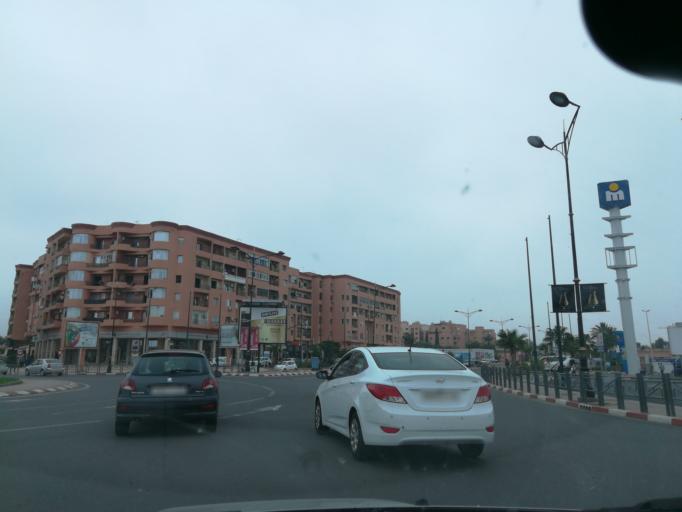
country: MA
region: Marrakech-Tensift-Al Haouz
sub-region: Marrakech
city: Marrakesh
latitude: 31.6674
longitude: -8.0115
